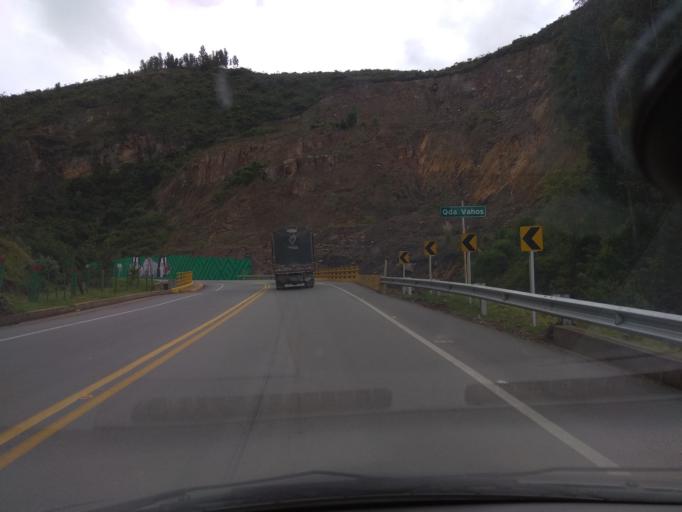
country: CO
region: Boyaca
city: Duitama
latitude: 5.8525
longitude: -73.0123
